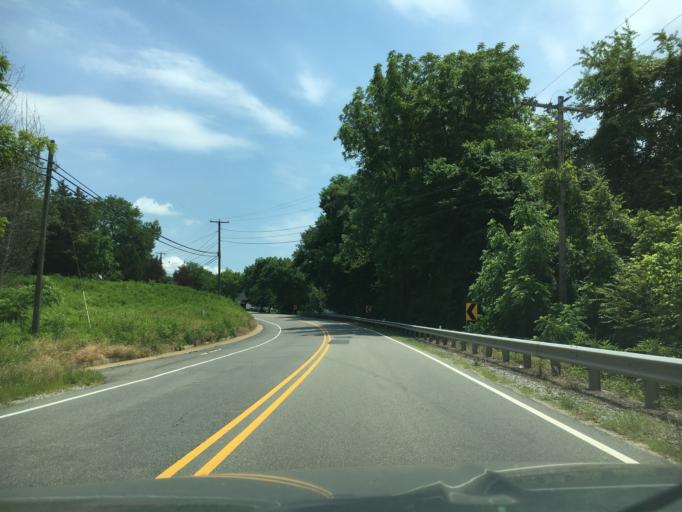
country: US
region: Virginia
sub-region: Buckingham County
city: Buckingham
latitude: 37.5502
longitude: -78.5608
